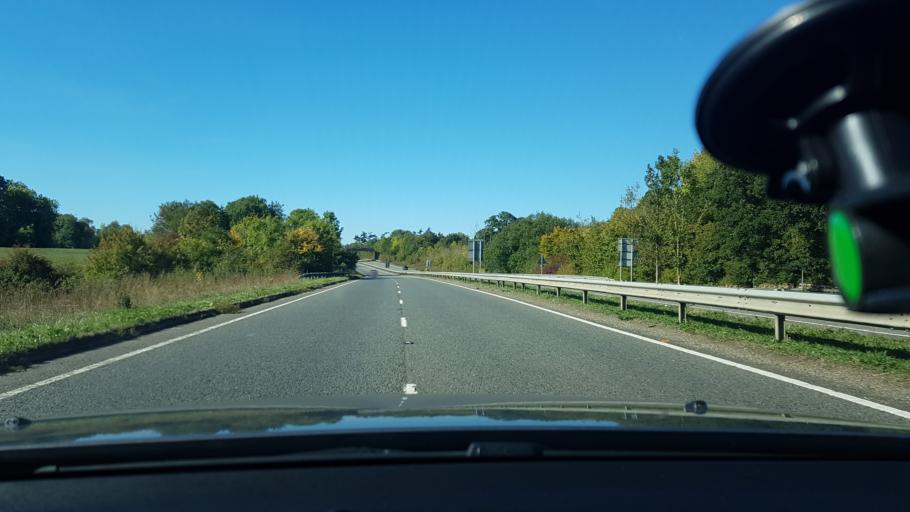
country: GB
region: England
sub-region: Hampshire
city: Kingsley
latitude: 51.1911
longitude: -0.8628
